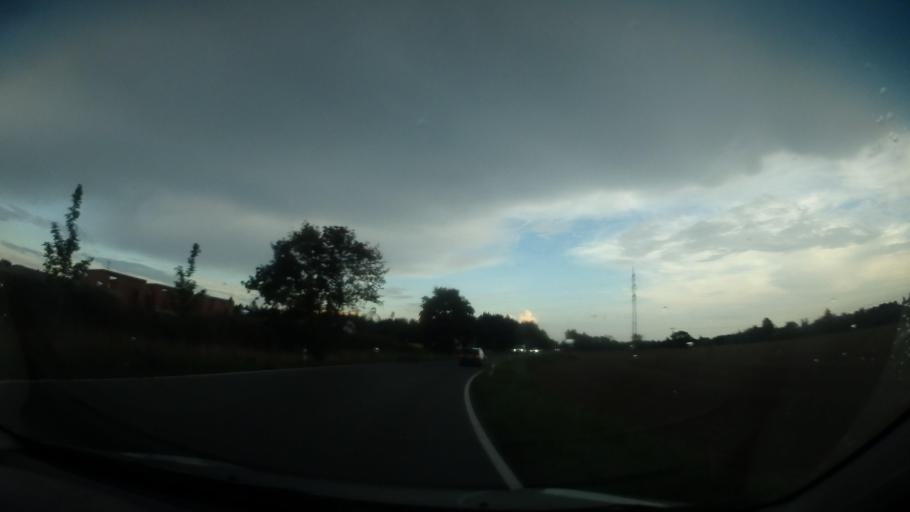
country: CZ
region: Olomoucky
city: Horka nad Moravou
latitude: 49.6310
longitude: 17.2399
